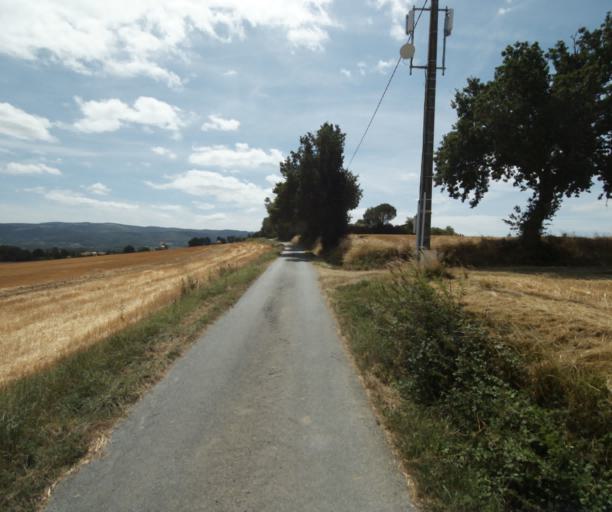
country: FR
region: Midi-Pyrenees
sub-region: Departement du Tarn
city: Soreze
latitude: 43.4930
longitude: 2.0675
